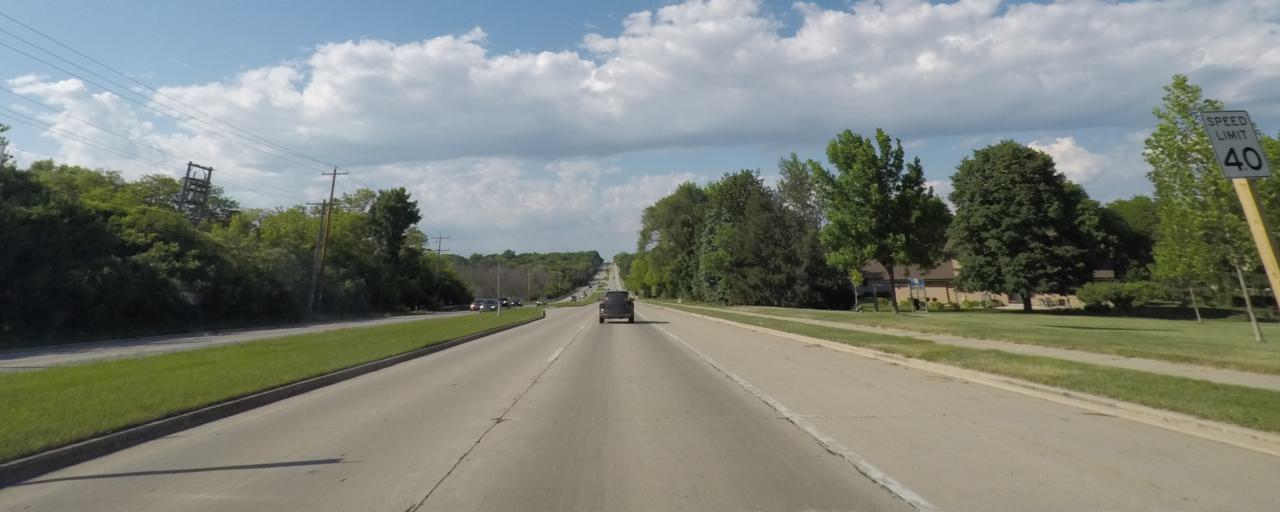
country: US
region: Wisconsin
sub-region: Milwaukee County
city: Greendale
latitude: 42.9240
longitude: -88.0089
